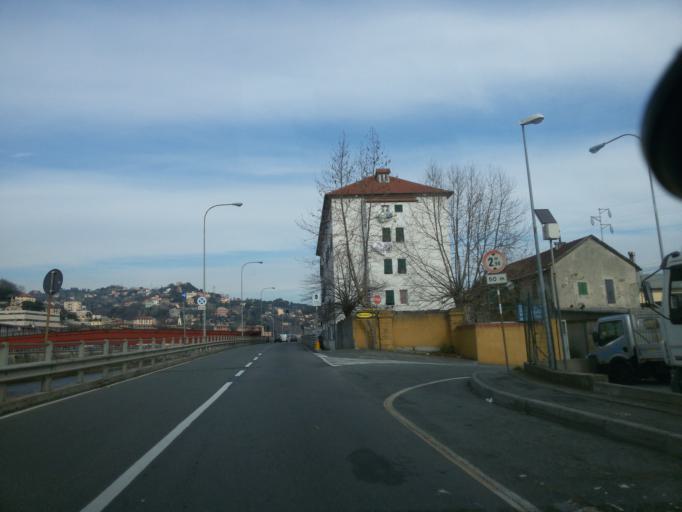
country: IT
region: Liguria
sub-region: Provincia di Genova
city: Genoa
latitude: 44.4456
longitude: 8.8905
